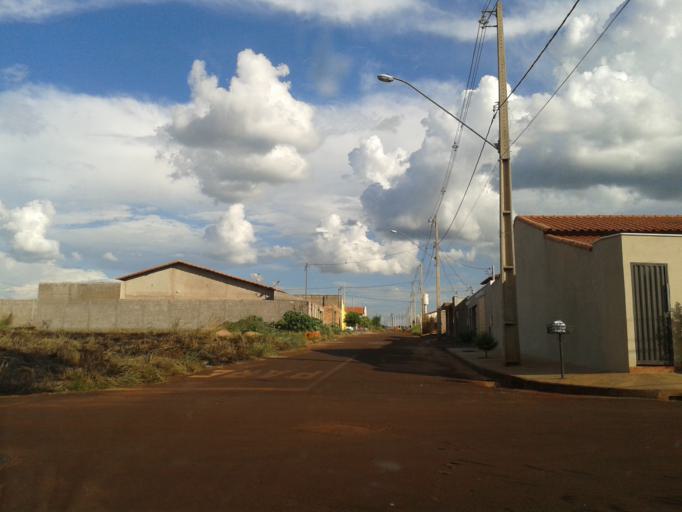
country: BR
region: Minas Gerais
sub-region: Capinopolis
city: Capinopolis
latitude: -18.6906
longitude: -49.5772
